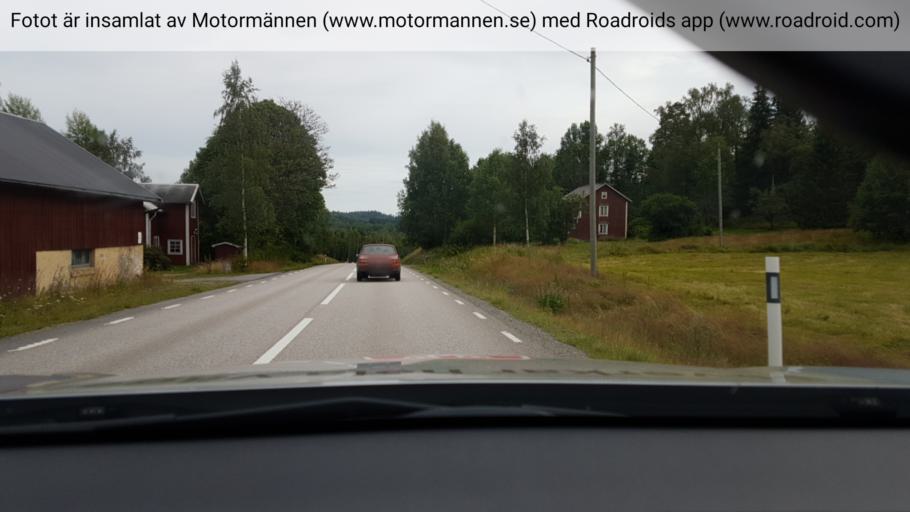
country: SE
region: Vaestra Goetaland
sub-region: Bengtsfors Kommun
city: Dals Langed
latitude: 58.8882
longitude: 12.2107
